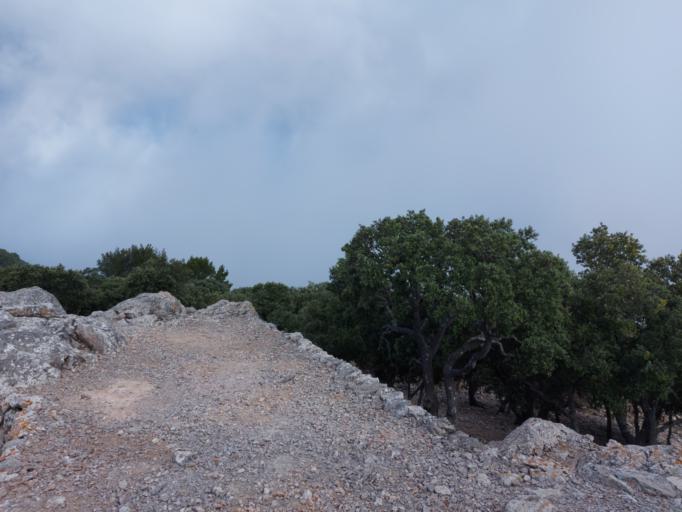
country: ES
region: Balearic Islands
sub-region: Illes Balears
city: Valldemossa
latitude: 39.7291
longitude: 2.6190
